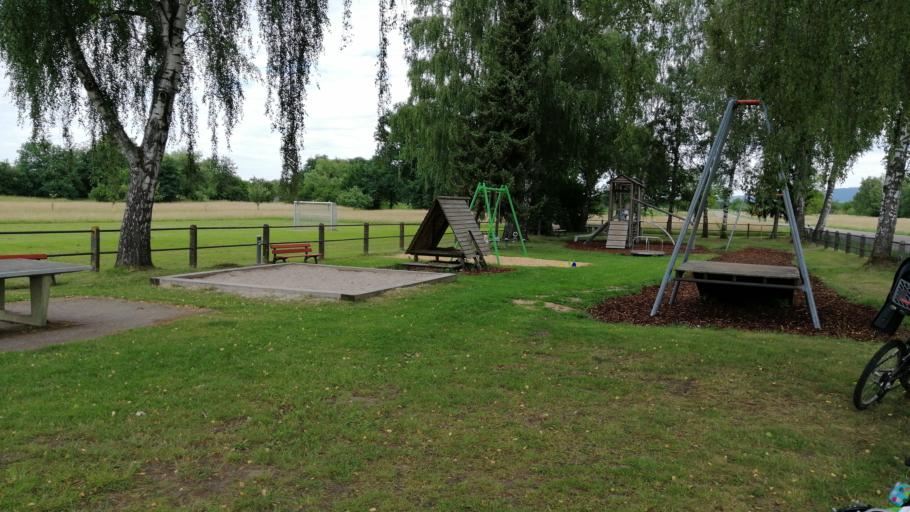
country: DE
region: Baden-Wuerttemberg
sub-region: Karlsruhe Region
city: Kuppenheim
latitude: 48.8268
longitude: 8.2332
